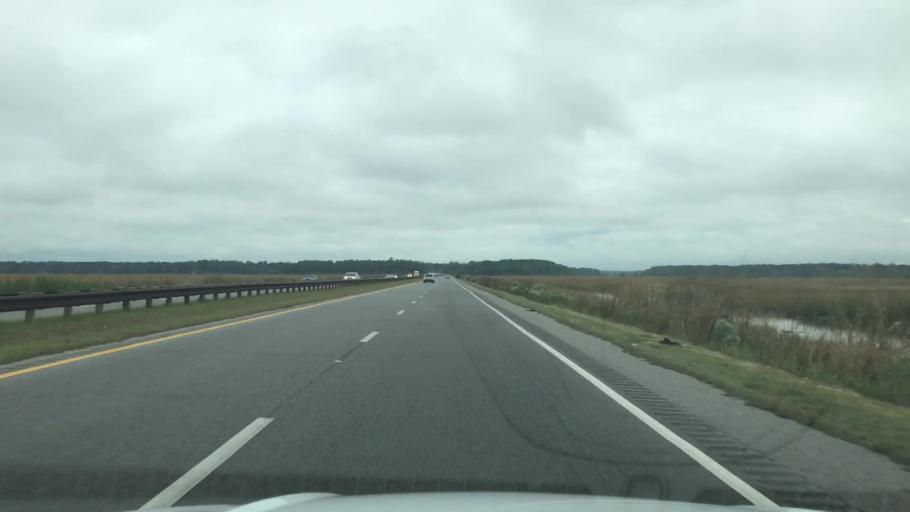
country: US
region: South Carolina
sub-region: Hampton County
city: Yemassee
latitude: 32.6585
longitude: -80.6668
